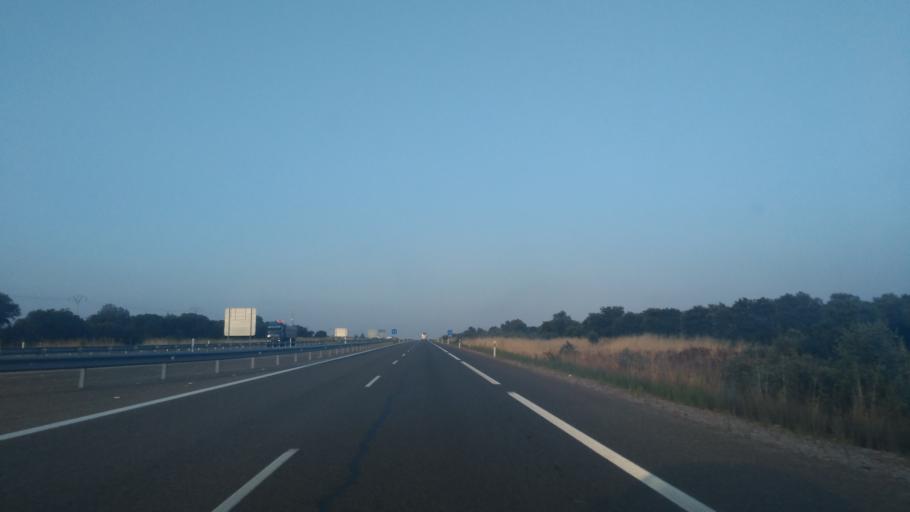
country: ES
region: Castille and Leon
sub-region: Provincia de Salamanca
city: Parada de Arriba
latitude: 40.9348
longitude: -5.7998
